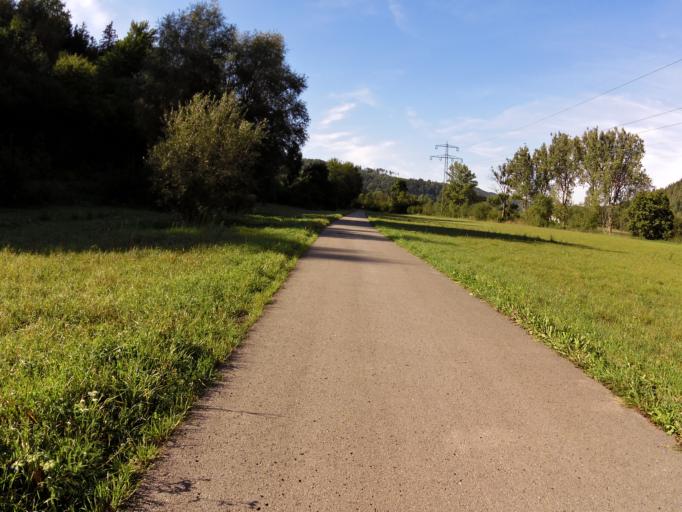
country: DE
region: Baden-Wuerttemberg
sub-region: Tuebingen Region
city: Hirrlingen
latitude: 48.4578
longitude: 8.8761
